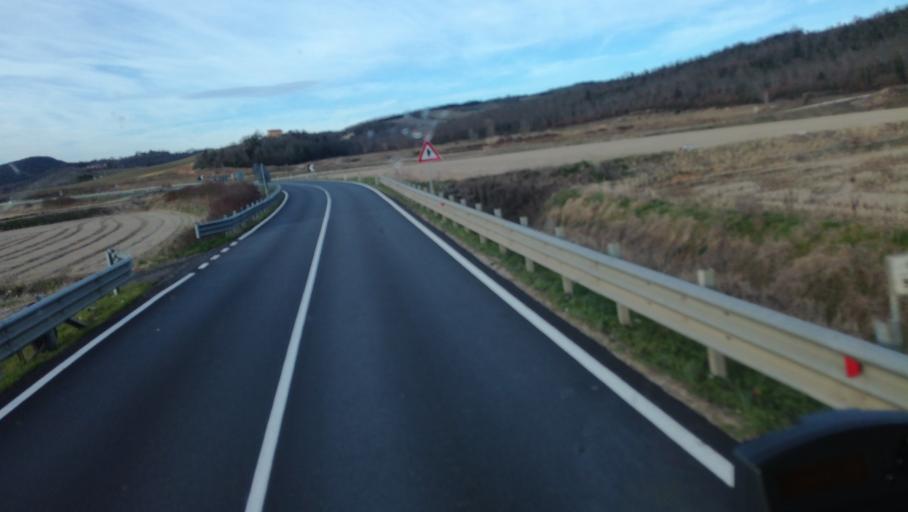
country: IT
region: Tuscany
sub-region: Provincia di Siena
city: Murlo
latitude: 43.1563
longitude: 11.2905
